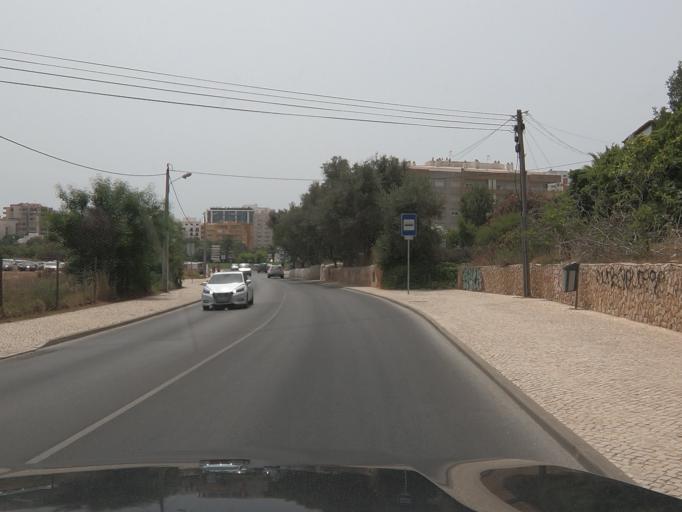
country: PT
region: Faro
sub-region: Portimao
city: Portimao
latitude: 37.1237
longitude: -8.5350
